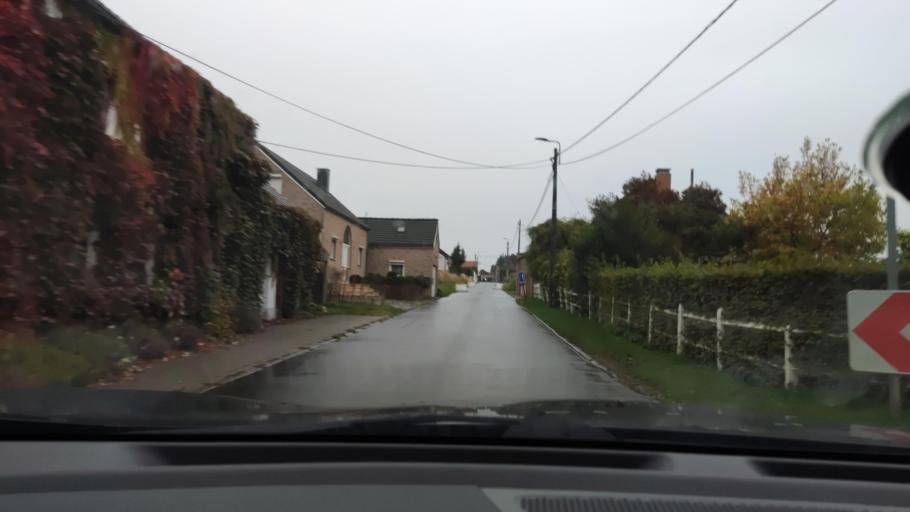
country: BE
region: Wallonia
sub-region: Province de Liege
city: Lincent
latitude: 50.7208
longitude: 4.9678
